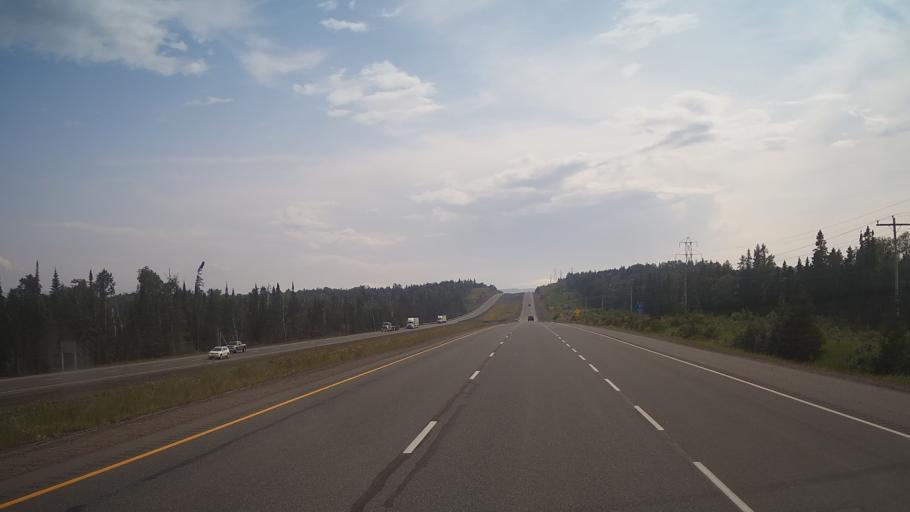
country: CA
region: Ontario
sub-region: Thunder Bay District
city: Thunder Bay
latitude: 48.6006
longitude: -88.7839
